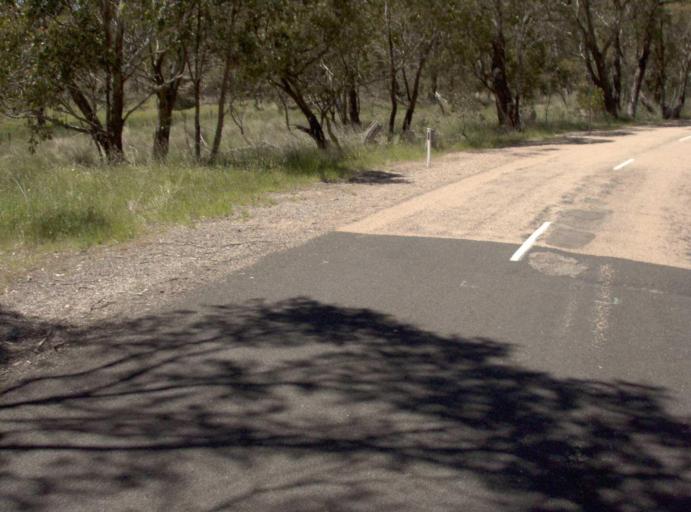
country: AU
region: Victoria
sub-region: East Gippsland
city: Lakes Entrance
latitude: -37.1374
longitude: 148.2441
